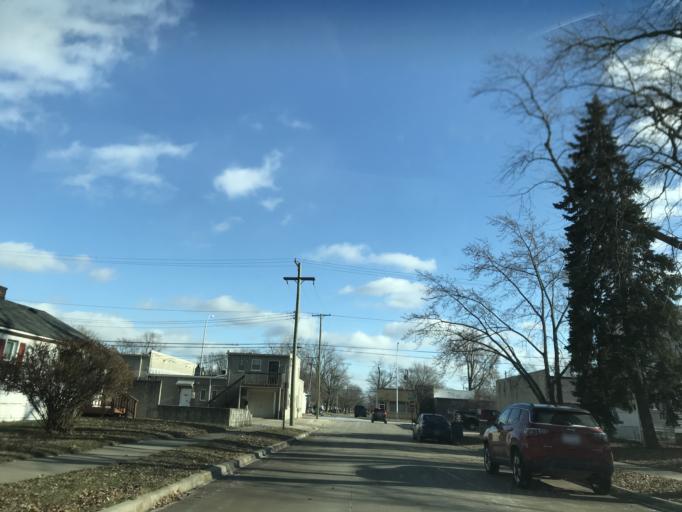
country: US
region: Michigan
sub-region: Oakland County
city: Madison Heights
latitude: 42.4791
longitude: -83.1060
